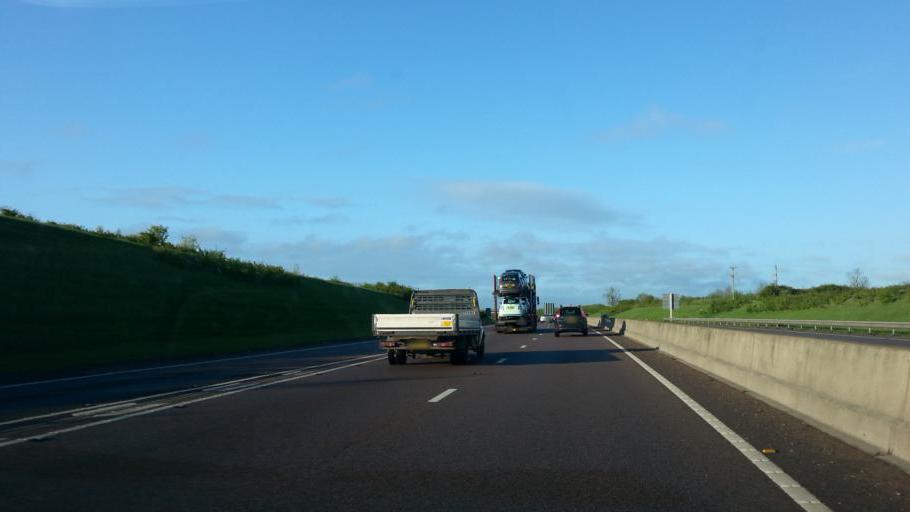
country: GB
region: England
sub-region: Nottinghamshire
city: Bingham
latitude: 52.9452
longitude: -0.9886
